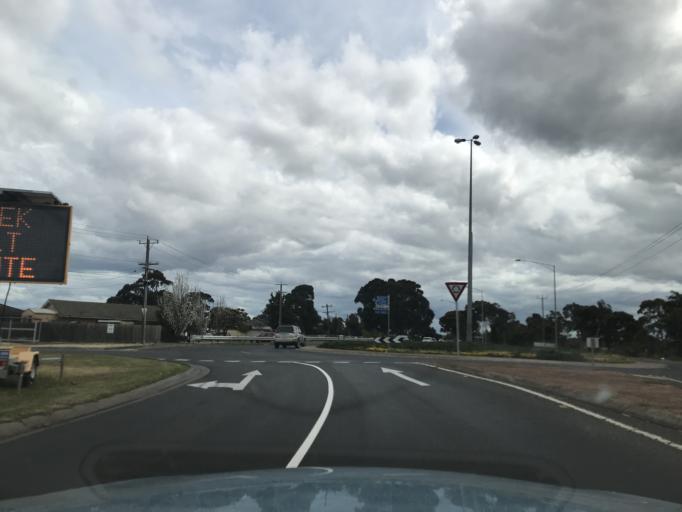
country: AU
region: Victoria
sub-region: Hobsons Bay
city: Laverton
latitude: -37.8483
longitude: 144.7736
